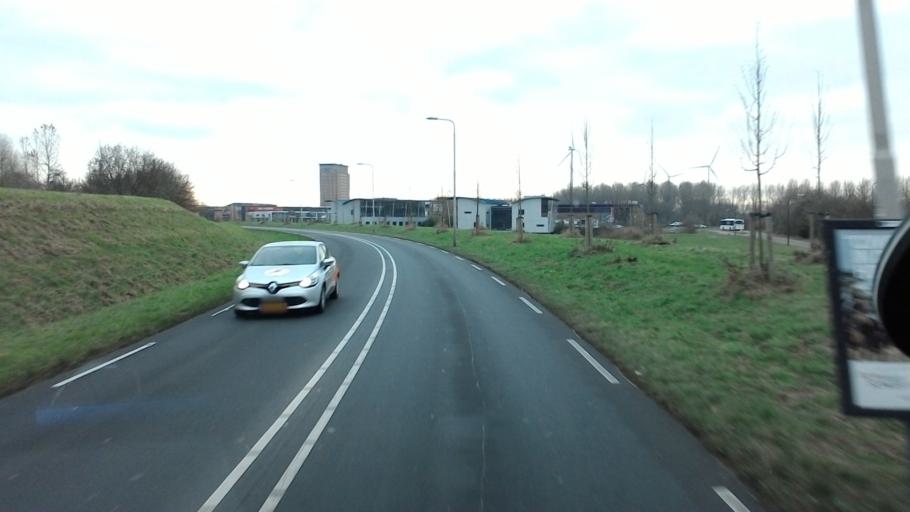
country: NL
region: Utrecht
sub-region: Gemeente Houten
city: Houten
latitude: 52.0327
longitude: 5.1424
